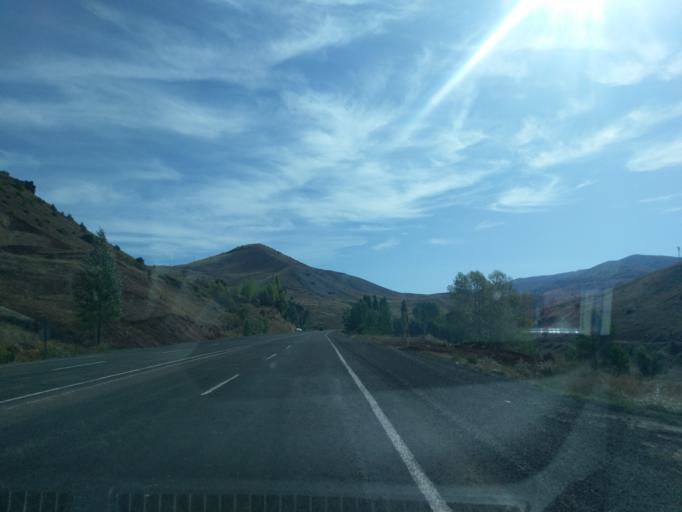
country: TR
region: Sivas
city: Akincilar
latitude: 39.8619
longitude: 38.3463
